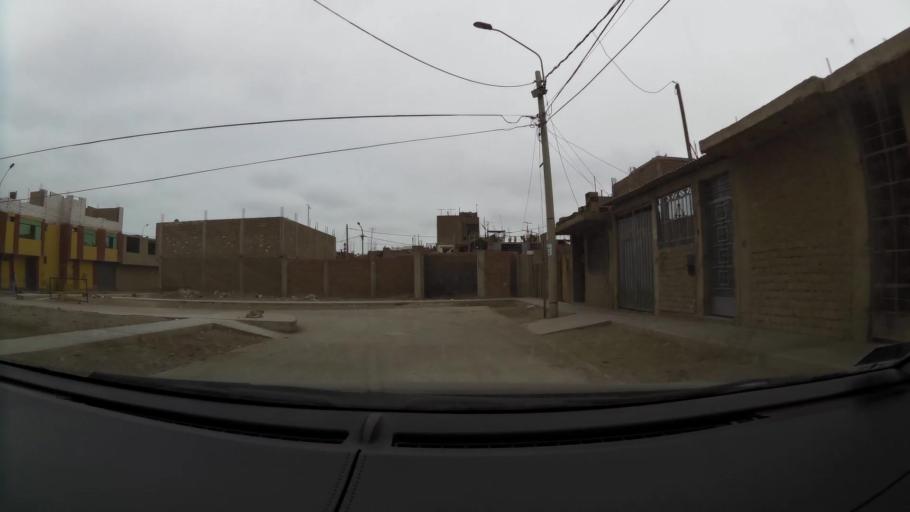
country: PE
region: Lima
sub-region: Lima
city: Independencia
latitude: -11.9737
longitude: -77.0928
